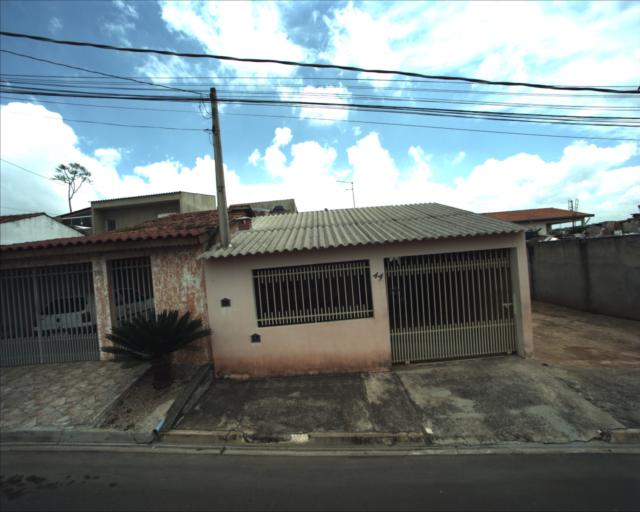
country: BR
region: Sao Paulo
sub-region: Sorocaba
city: Sorocaba
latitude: -23.4180
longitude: -47.4313
